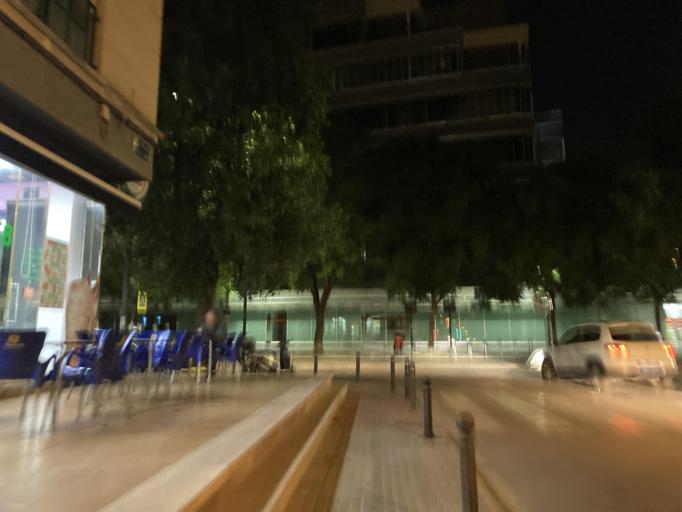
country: ES
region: Murcia
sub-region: Murcia
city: Murcia
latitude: 37.9980
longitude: -1.1312
